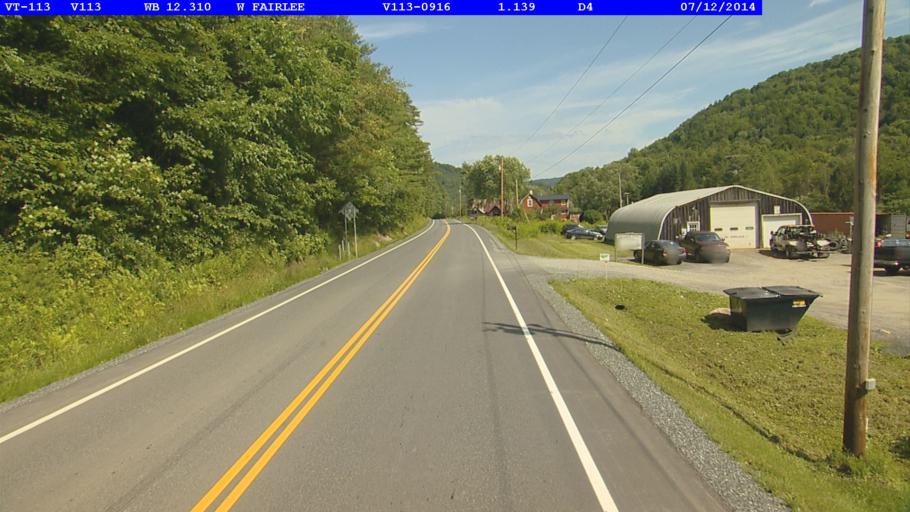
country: US
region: New Hampshire
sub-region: Grafton County
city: Orford
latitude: 43.9211
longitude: -72.2635
